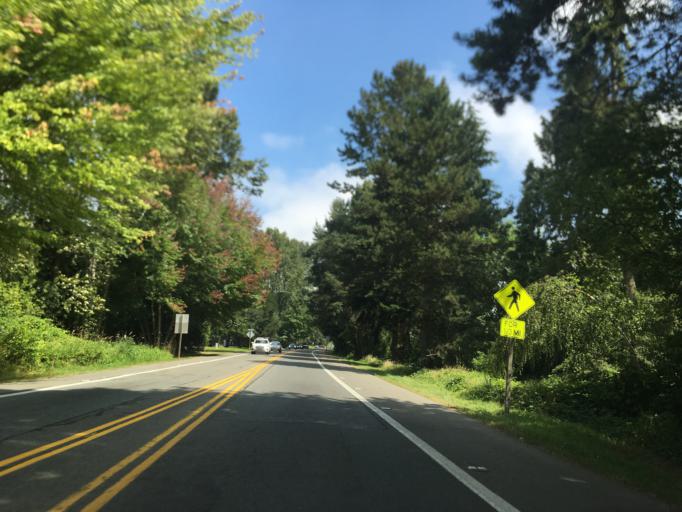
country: US
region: Washington
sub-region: King County
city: Kingsgate
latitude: 47.7337
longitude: -122.1947
